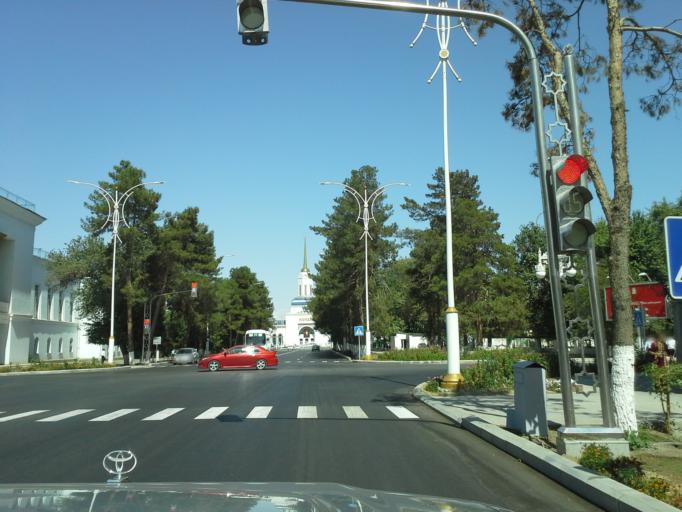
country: TM
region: Ahal
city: Ashgabat
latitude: 37.9405
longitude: 58.3936
